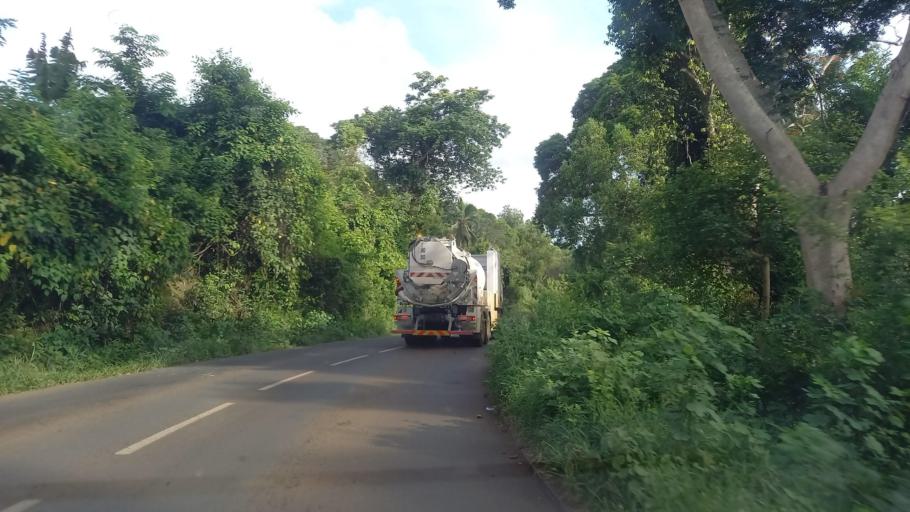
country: YT
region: Chiconi
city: Chiconi
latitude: -12.8203
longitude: 45.1288
